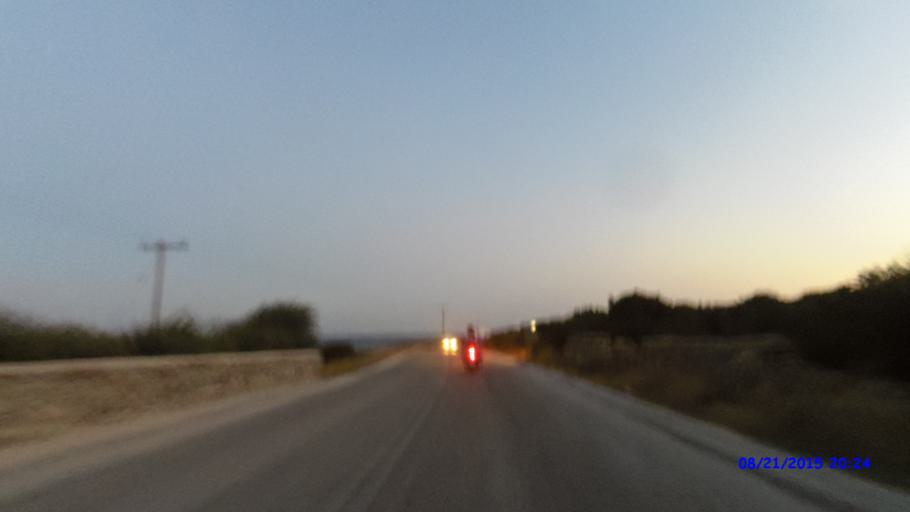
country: GR
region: South Aegean
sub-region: Nomos Kykladon
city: Antiparos
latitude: 36.9881
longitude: 25.0722
